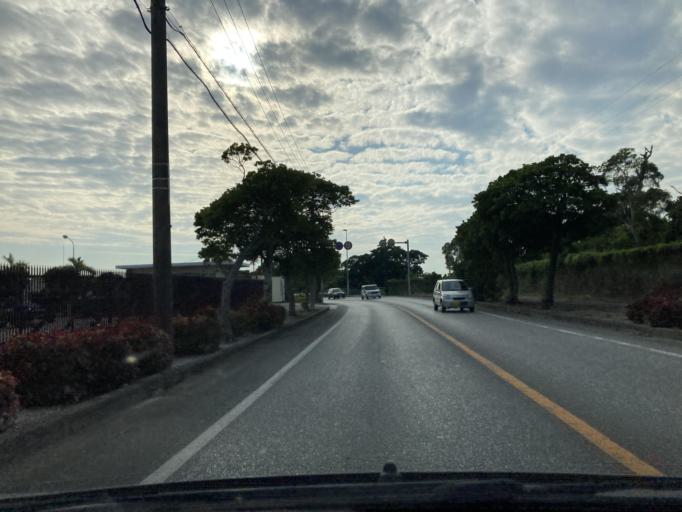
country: JP
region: Okinawa
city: Okinawa
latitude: 26.3660
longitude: 127.7986
